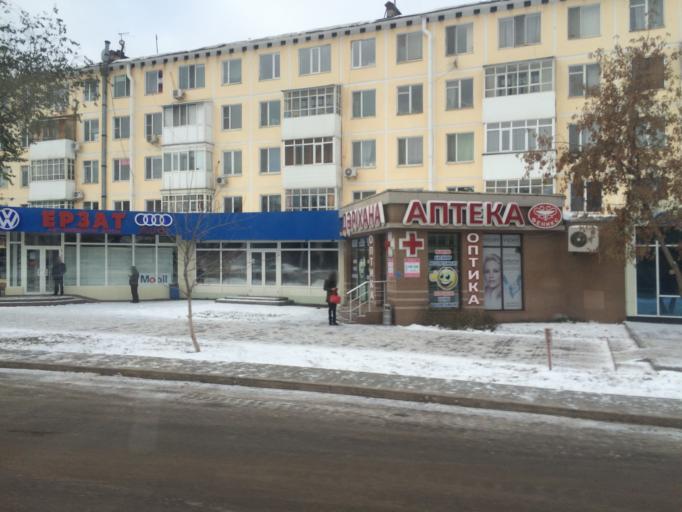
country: KZ
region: Astana Qalasy
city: Astana
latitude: 51.1735
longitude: 71.4192
